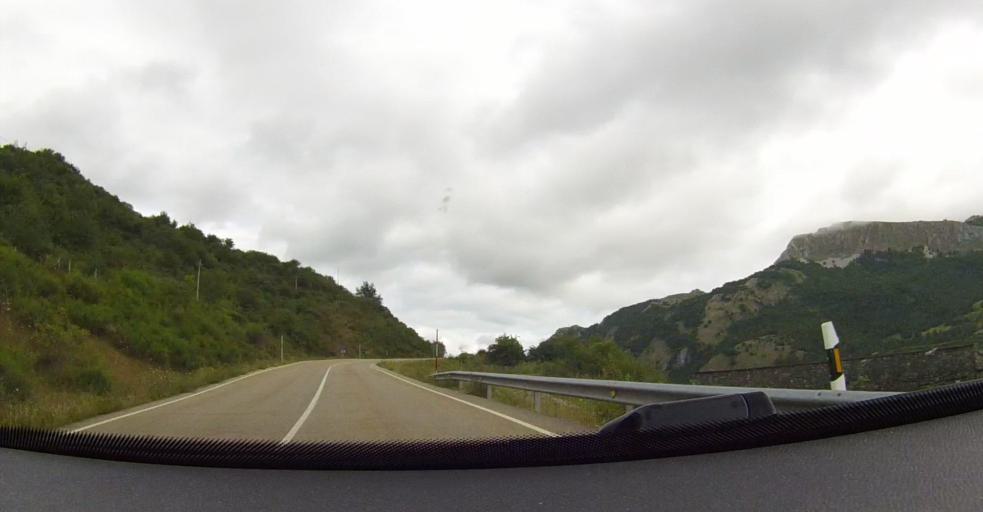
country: ES
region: Castille and Leon
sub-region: Provincia de Leon
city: Buron
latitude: 43.0229
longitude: -5.0432
